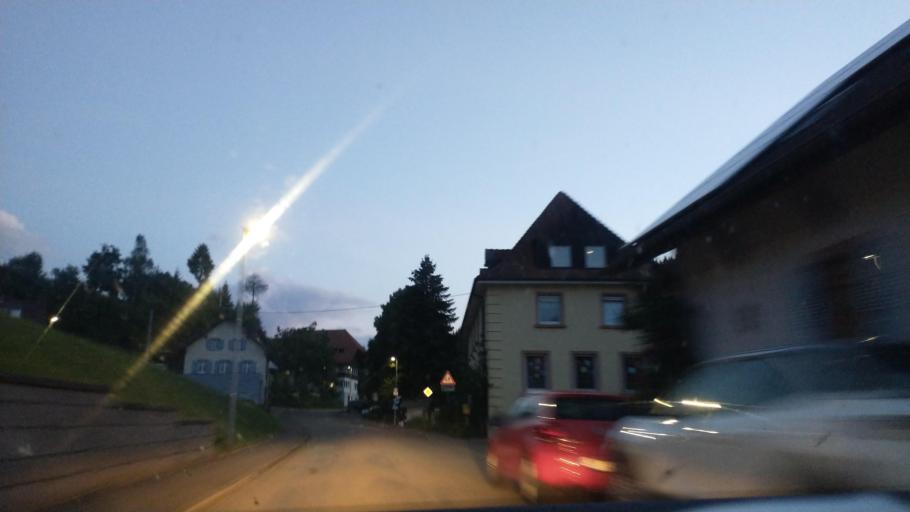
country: DE
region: Baden-Wuerttemberg
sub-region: Freiburg Region
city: Biberach
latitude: 48.3204
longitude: 8.0025
